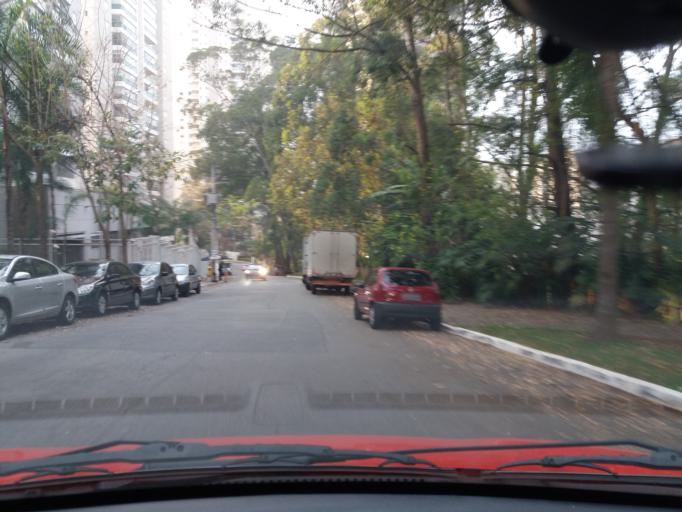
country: BR
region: Sao Paulo
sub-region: Taboao Da Serra
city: Taboao da Serra
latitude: -23.6265
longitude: -46.7398
